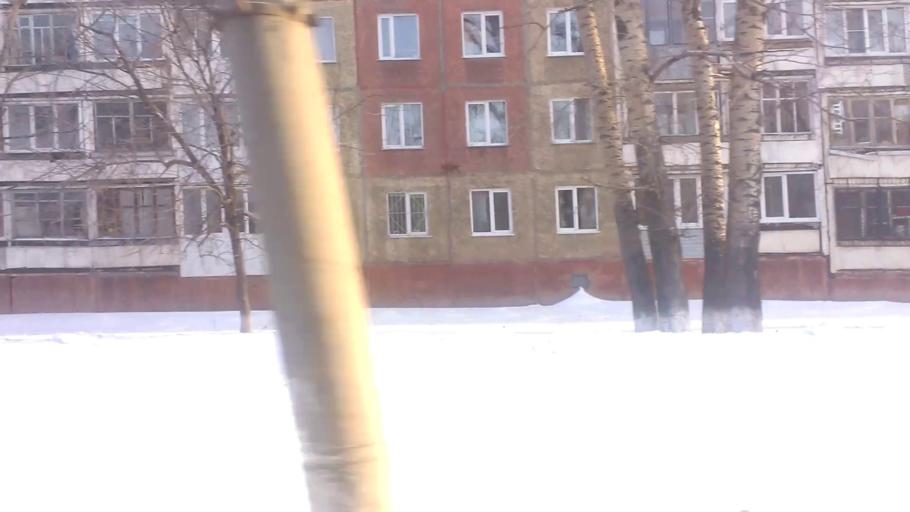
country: RU
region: Altai Krai
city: Novosilikatnyy
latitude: 53.3726
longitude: 83.6631
